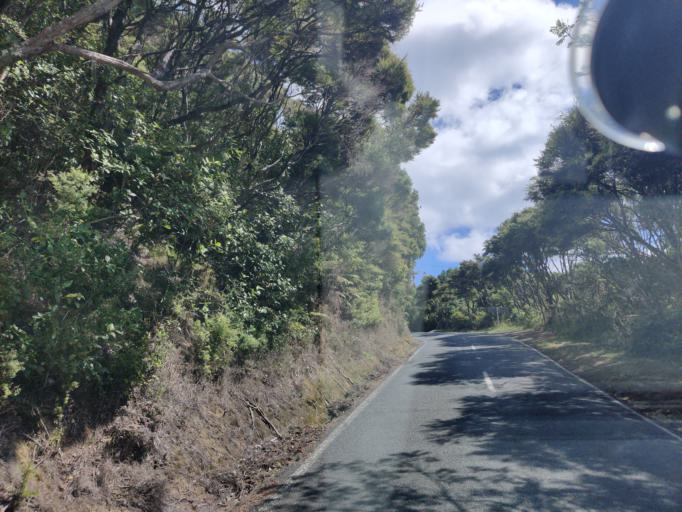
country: NZ
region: Northland
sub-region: Far North District
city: Paihia
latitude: -35.2575
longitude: 174.2393
